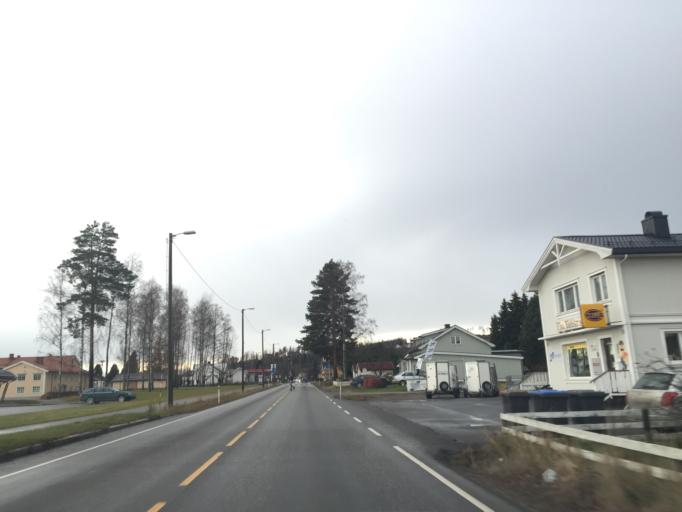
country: NO
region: Hedmark
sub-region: Asnes
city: Flisa
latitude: 60.6132
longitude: 12.0182
